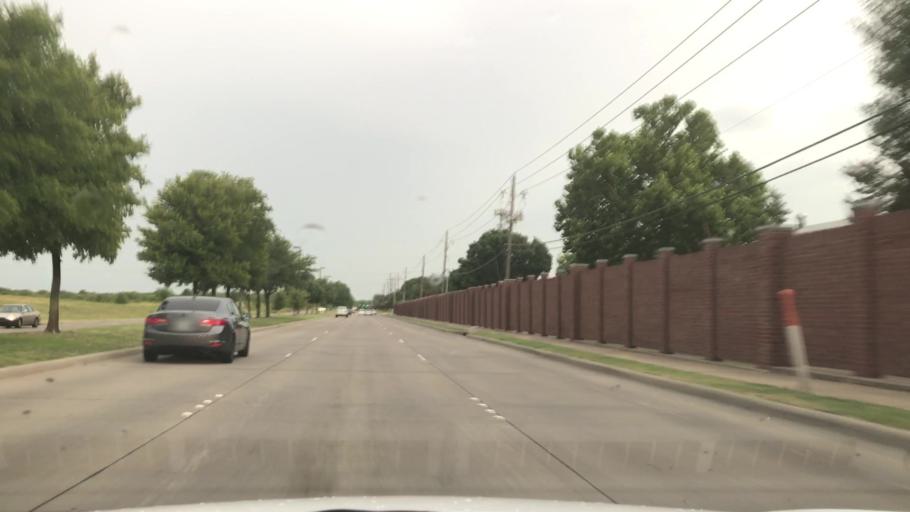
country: US
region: Texas
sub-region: Dallas County
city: Mesquite
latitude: 32.7441
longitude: -96.5795
